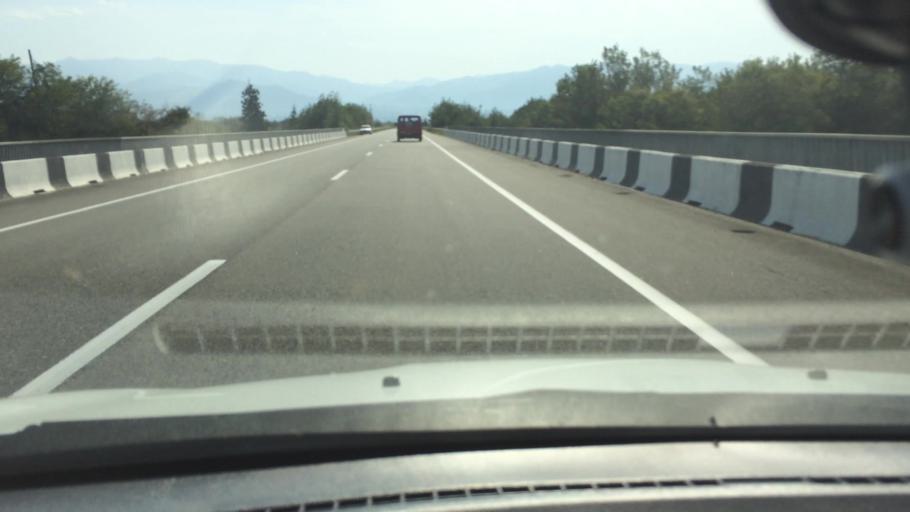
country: GE
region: Ajaria
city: Ochkhamuri
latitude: 41.9095
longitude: 41.7836
